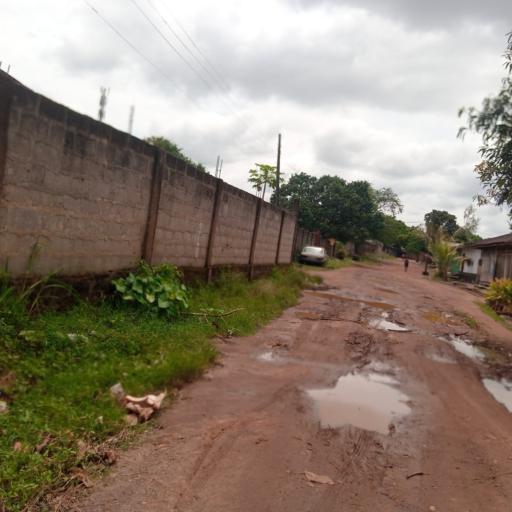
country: SL
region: Eastern Province
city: Kenema
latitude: 7.8853
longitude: -11.1898
